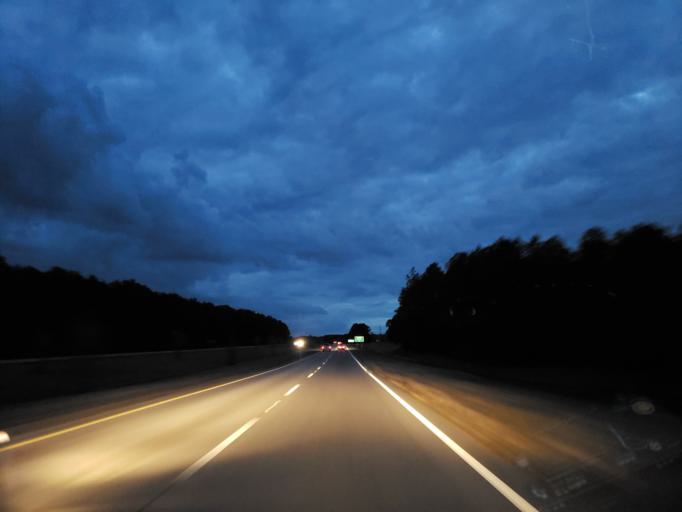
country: US
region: Mississippi
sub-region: Forrest County
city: Hattiesburg
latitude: 31.2454
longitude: -89.2580
